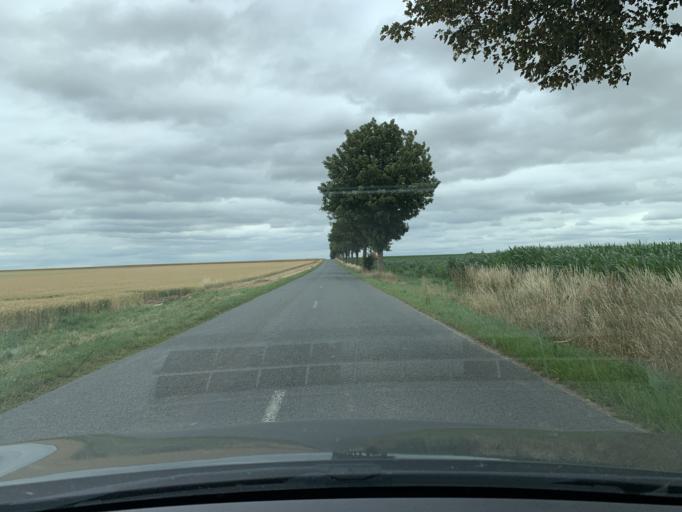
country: FR
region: Nord-Pas-de-Calais
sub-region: Departement du Pas-de-Calais
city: Oisy-le-Verger
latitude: 50.2275
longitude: 3.1410
